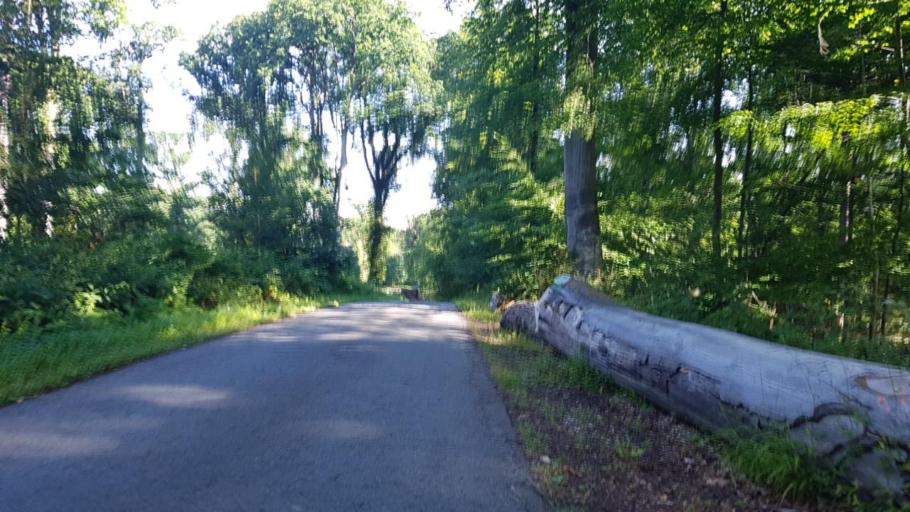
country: FR
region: Picardie
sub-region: Departement de l'Oise
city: Fleurines
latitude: 49.2638
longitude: 2.6184
